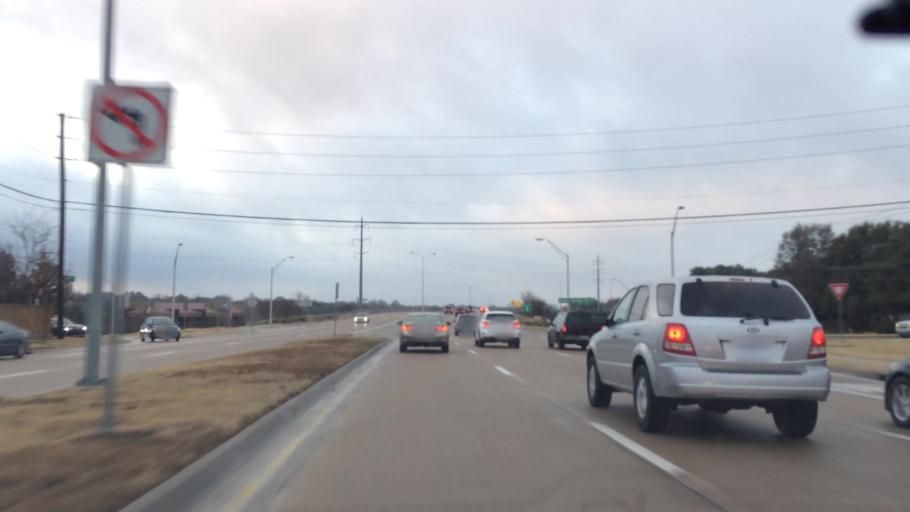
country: US
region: Texas
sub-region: Dallas County
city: Addison
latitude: 32.9732
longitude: -96.8043
